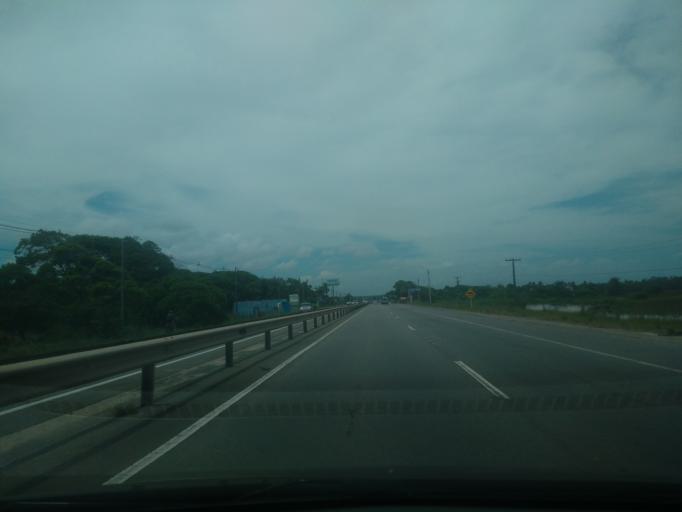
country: BR
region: Alagoas
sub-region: Marechal Deodoro
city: Marechal Deodoro
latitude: -9.7608
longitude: -35.8441
